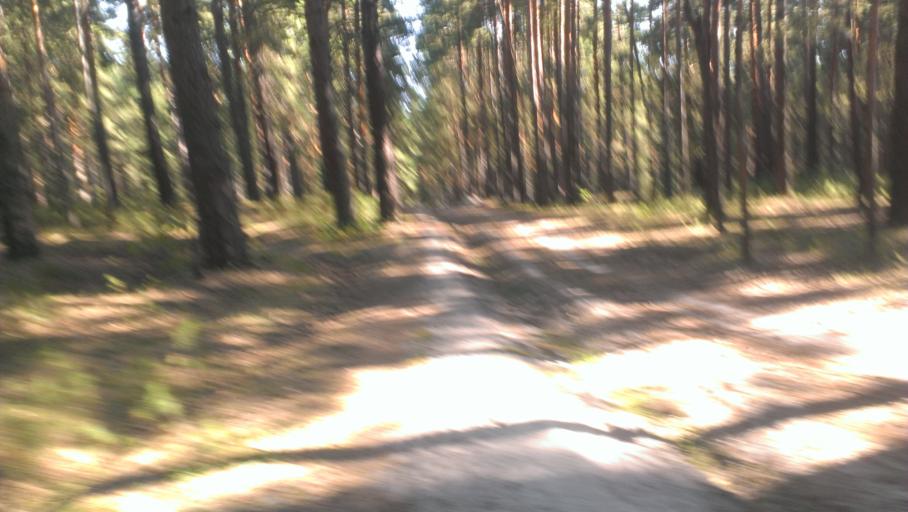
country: RU
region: Altai Krai
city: Novosilikatnyy
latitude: 53.3179
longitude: 83.6870
